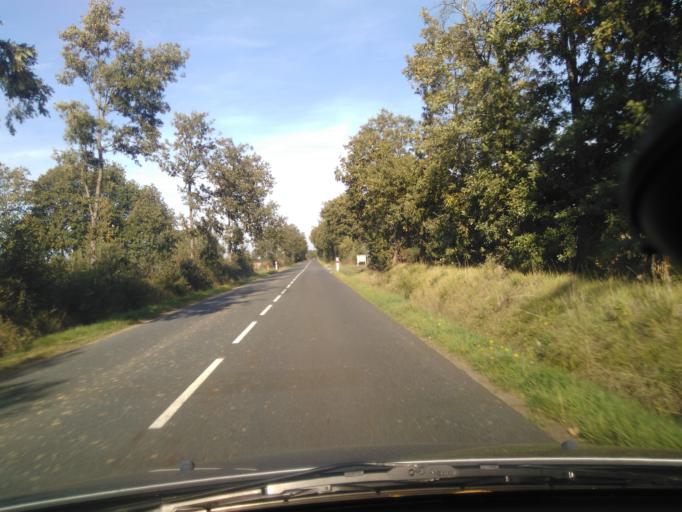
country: FR
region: Pays de la Loire
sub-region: Departement de la Vendee
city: Saint-Hilaire-de-Talmont
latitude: 46.4795
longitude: -1.5937
